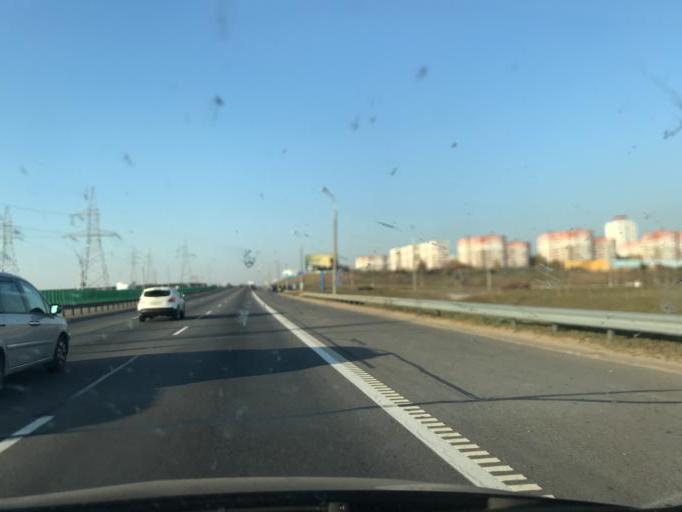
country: BY
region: Minsk
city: Malinovka
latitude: 53.8768
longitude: 27.4192
